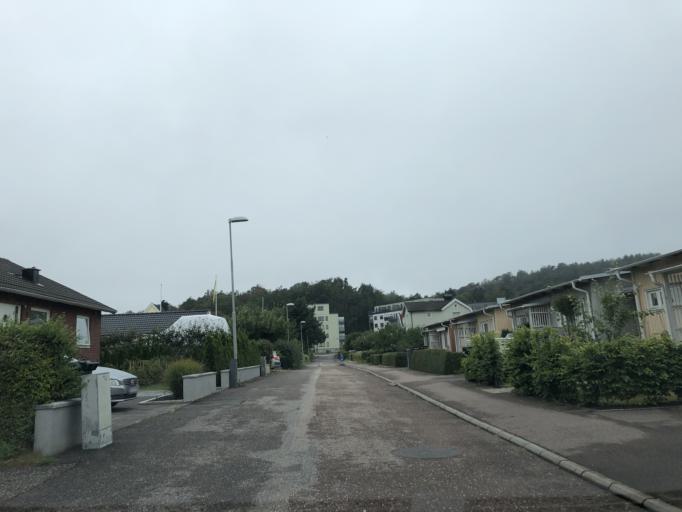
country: SE
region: Vaestra Goetaland
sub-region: Goteborg
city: Goeteborg
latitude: 57.7298
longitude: 11.9392
